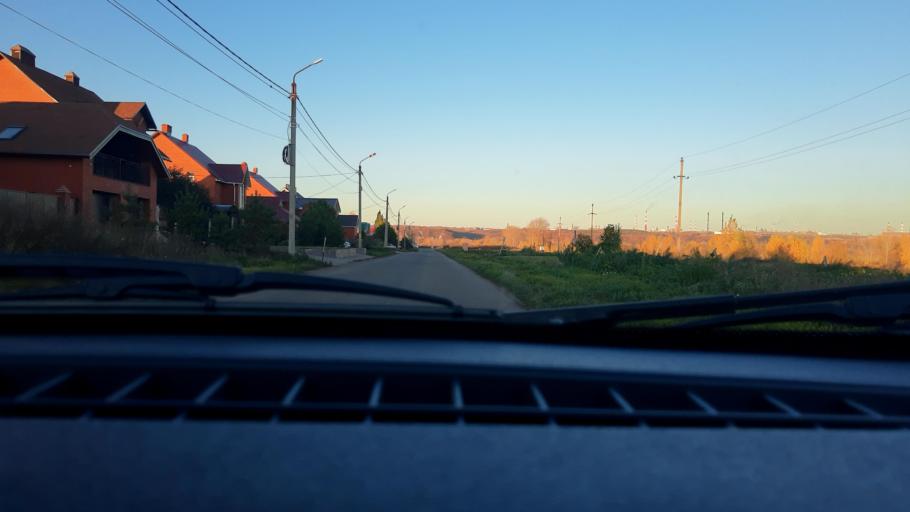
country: RU
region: Bashkortostan
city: Ufa
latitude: 54.8550
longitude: 56.0187
